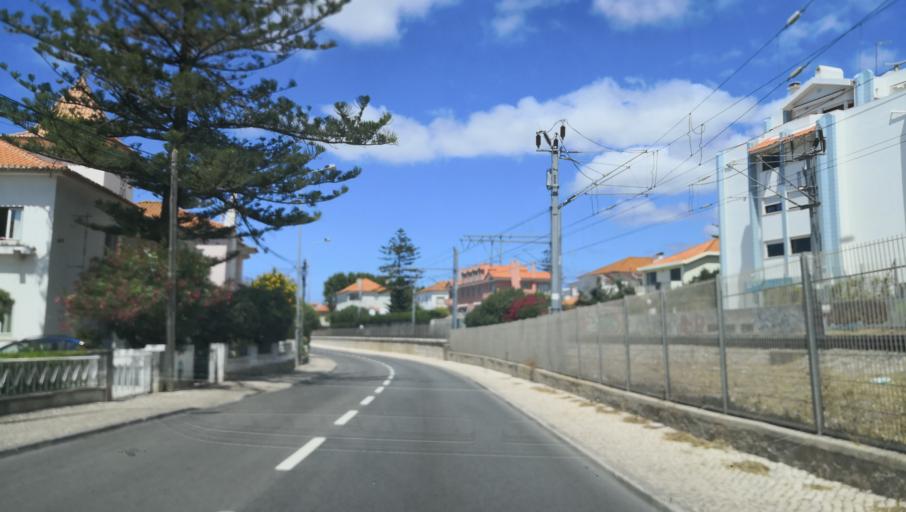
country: PT
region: Lisbon
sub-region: Cascais
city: Parede
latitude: 38.6902
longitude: -9.3579
